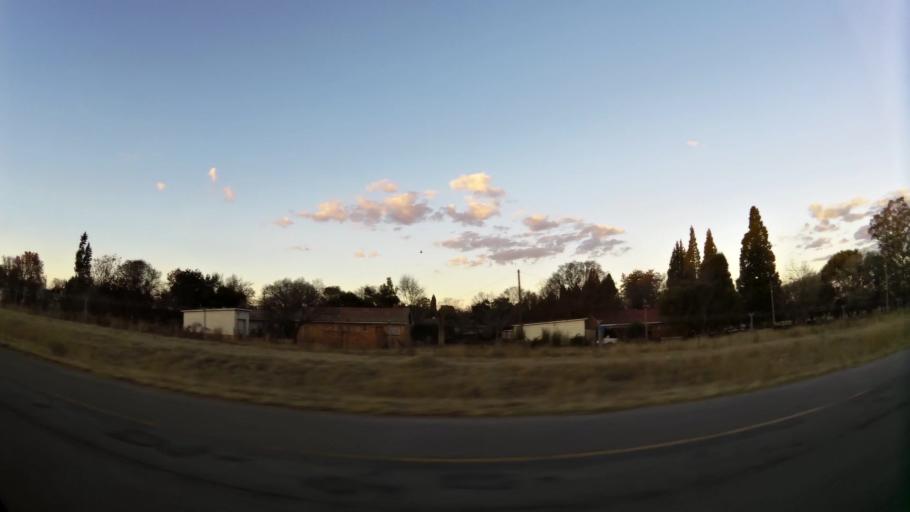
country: ZA
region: North-West
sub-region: Dr Kenneth Kaunda District Municipality
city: Potchefstroom
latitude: -26.6856
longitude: 27.0765
